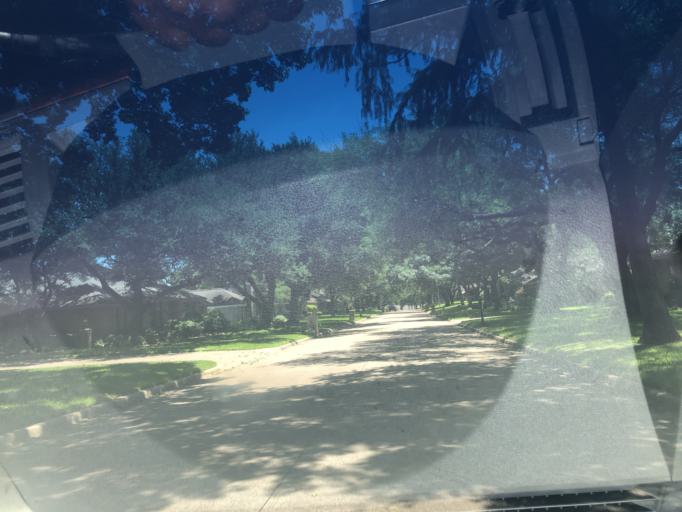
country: US
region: Texas
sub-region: Dallas County
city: Grand Prairie
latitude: 32.7795
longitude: -97.0420
